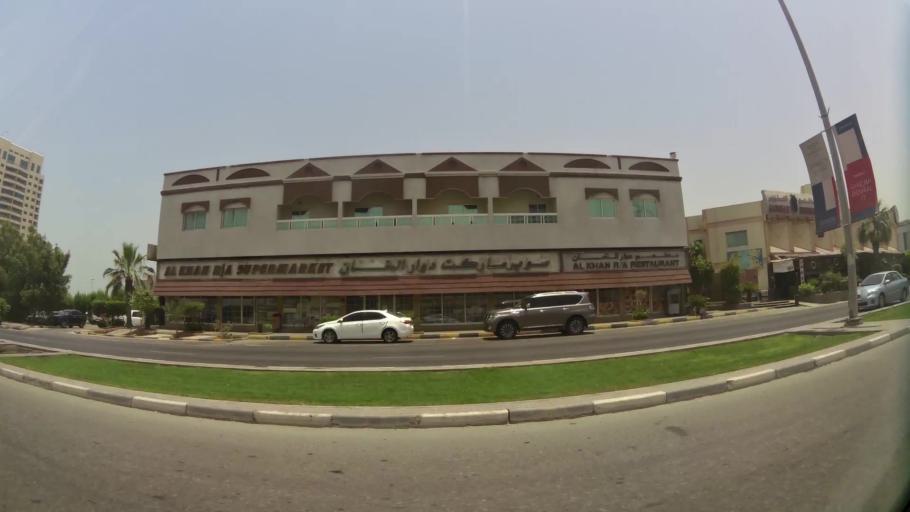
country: AE
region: Ash Shariqah
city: Sharjah
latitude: 25.3342
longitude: 55.3620
